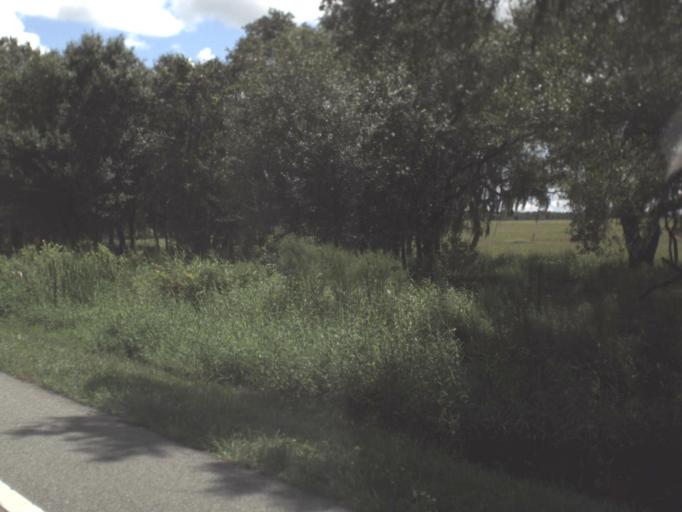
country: US
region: Florida
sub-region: Sarasota County
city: Lake Sarasota
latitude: 27.3566
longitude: -82.1819
